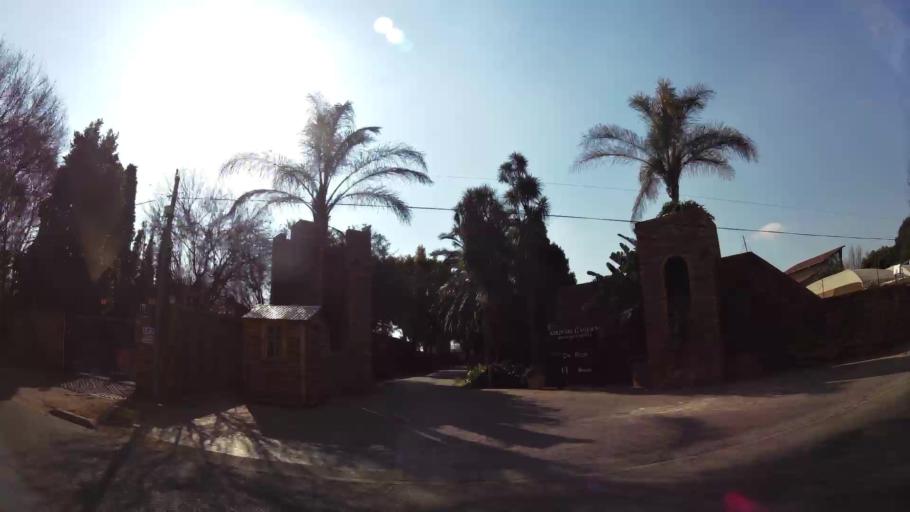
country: ZA
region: Gauteng
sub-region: Ekurhuleni Metropolitan Municipality
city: Boksburg
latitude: -26.1873
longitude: 28.2553
